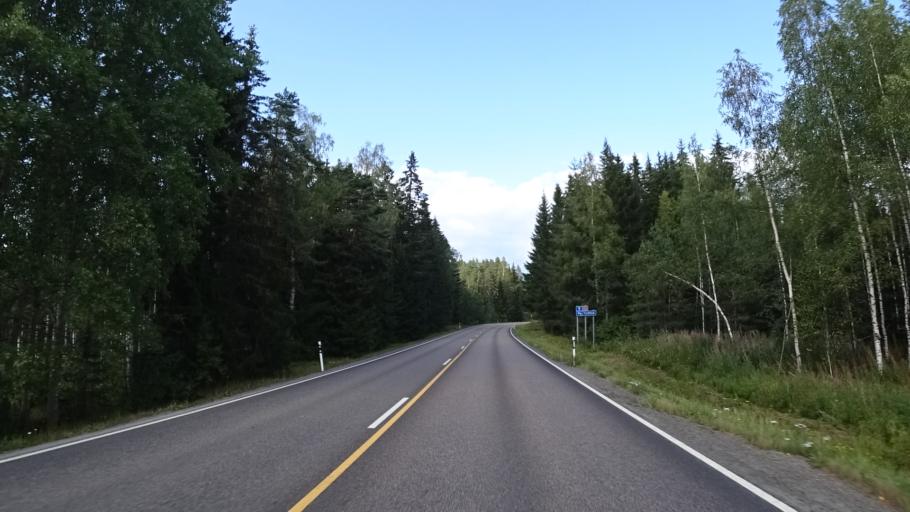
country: FI
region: Kymenlaakso
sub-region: Kotka-Hamina
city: Hamina
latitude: 60.7435
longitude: 27.3306
